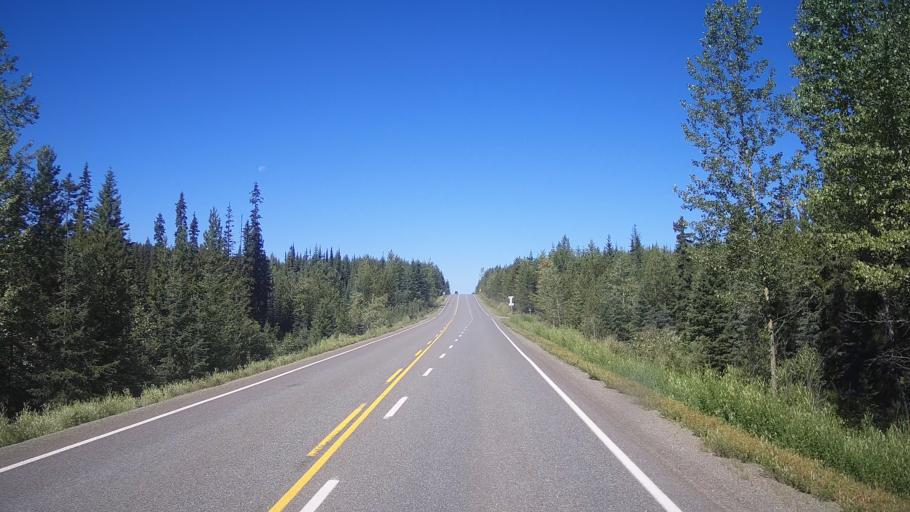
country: CA
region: British Columbia
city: Kamloops
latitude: 51.4978
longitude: -120.3684
